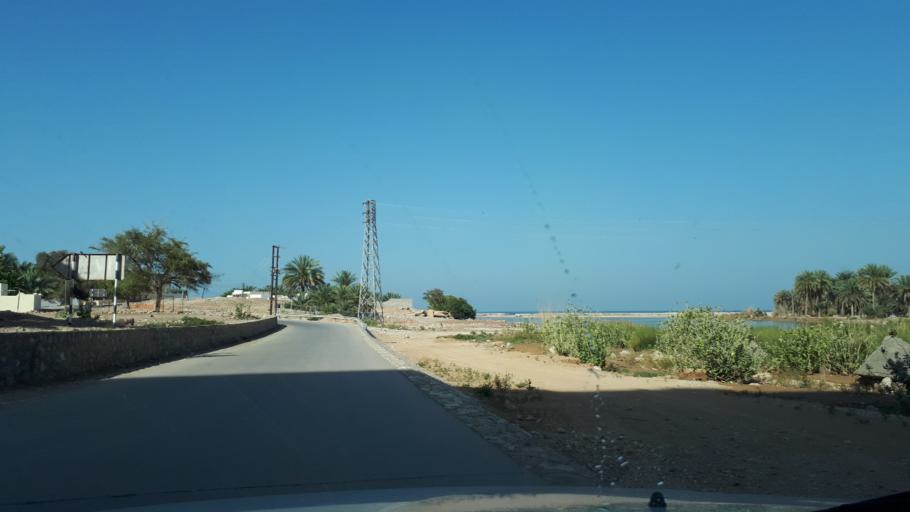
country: OM
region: Ash Sharqiyah
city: Sur
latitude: 22.8250
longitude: 59.2606
